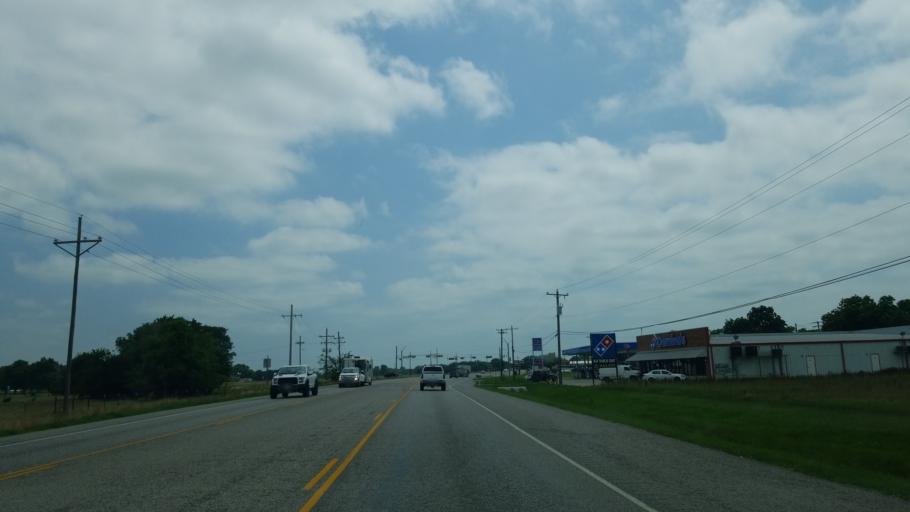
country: US
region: Texas
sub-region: Denton County
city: Pilot Point
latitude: 33.3972
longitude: -96.9454
